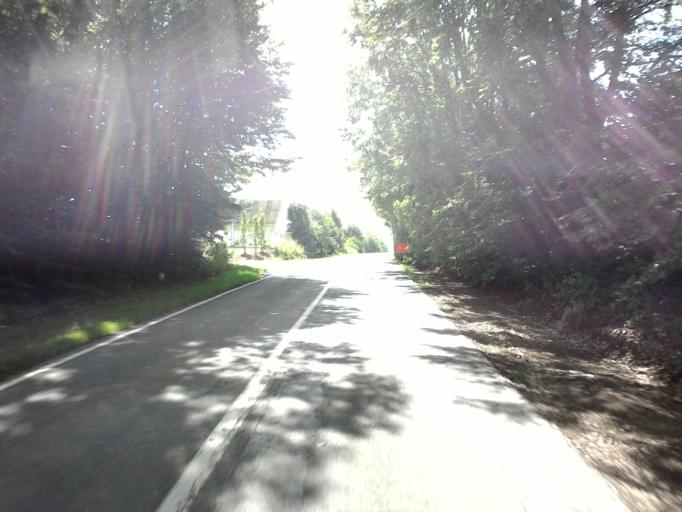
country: BE
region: Wallonia
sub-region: Province du Luxembourg
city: Habay-la-Vieille
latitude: 49.7701
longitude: 5.6221
